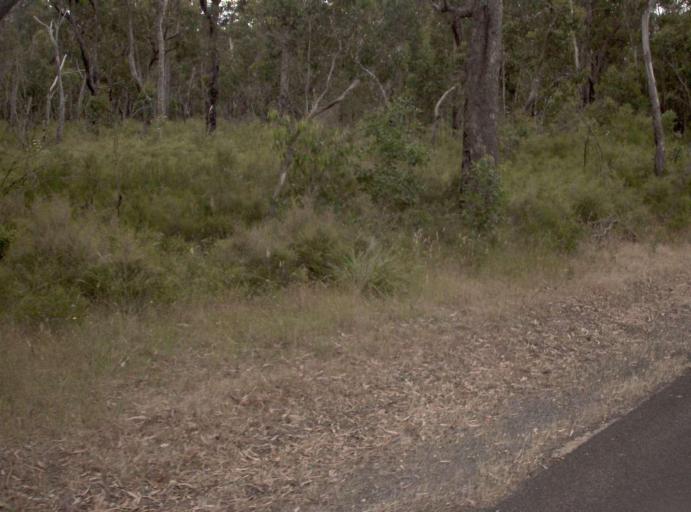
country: AU
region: Victoria
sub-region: Wellington
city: Sale
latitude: -38.3956
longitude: 146.9724
